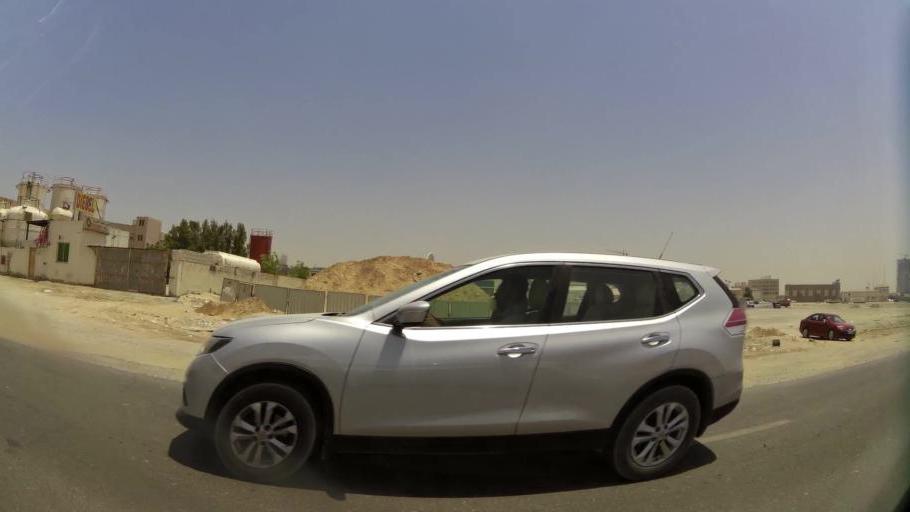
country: AE
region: Ajman
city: Ajman
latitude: 25.3982
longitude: 55.4991
